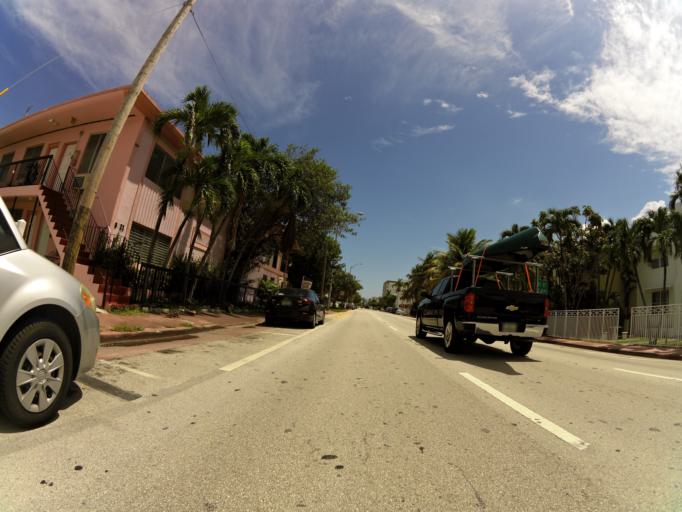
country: US
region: Florida
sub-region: Miami-Dade County
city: Surfside
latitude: 25.8676
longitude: -80.1223
